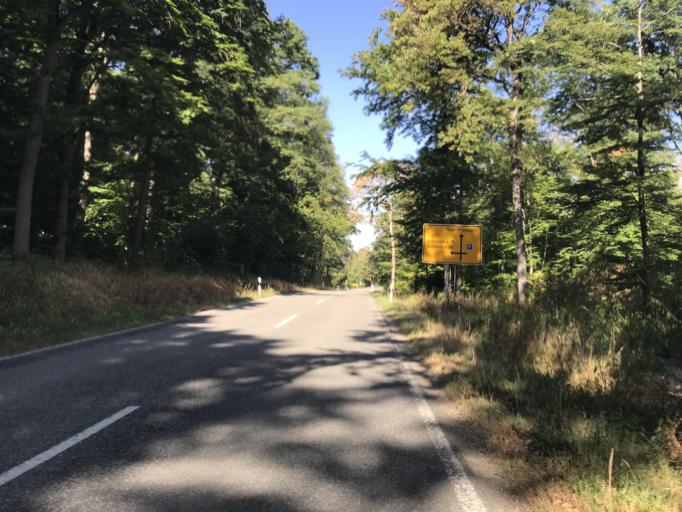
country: DE
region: Hesse
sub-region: Regierungsbezirk Darmstadt
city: Rudesheim am Rhein
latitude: 50.0462
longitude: 7.9294
